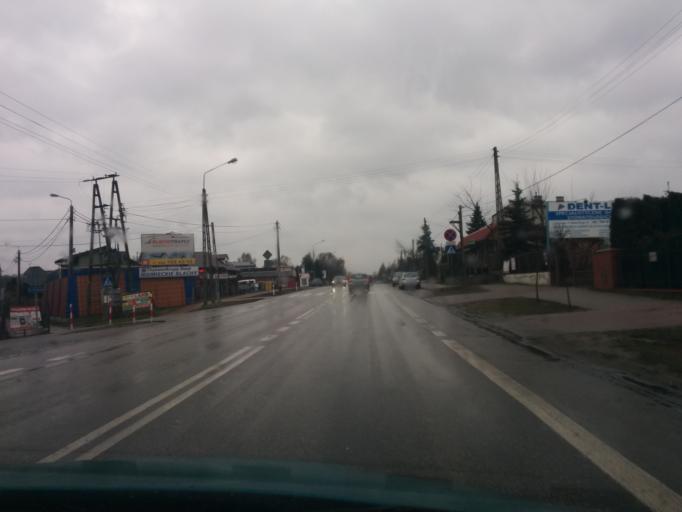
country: PL
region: Masovian Voivodeship
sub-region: Powiat legionowski
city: Jablonna
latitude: 52.3696
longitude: 20.9295
